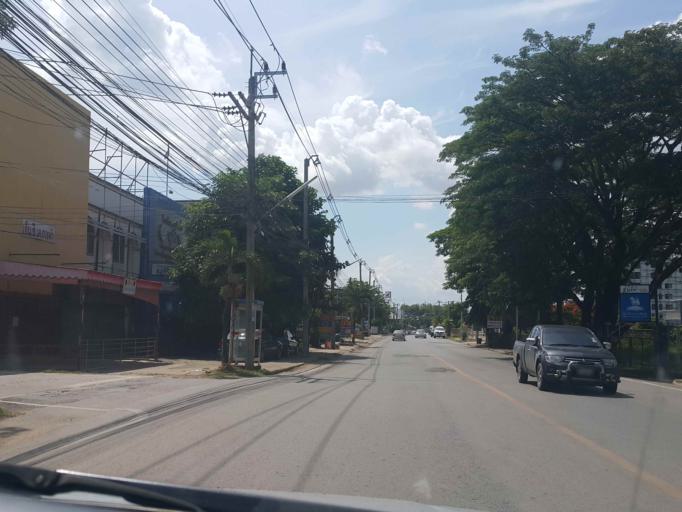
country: TH
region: Phayao
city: Phayao
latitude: 19.1653
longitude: 99.9086
